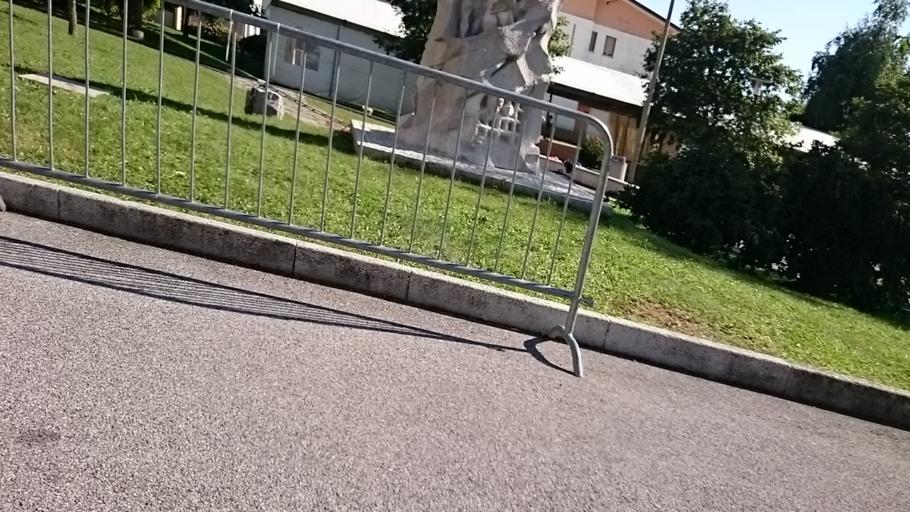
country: IT
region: Veneto
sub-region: Provincia di Belluno
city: Soverzene
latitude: 46.2043
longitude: 12.3027
